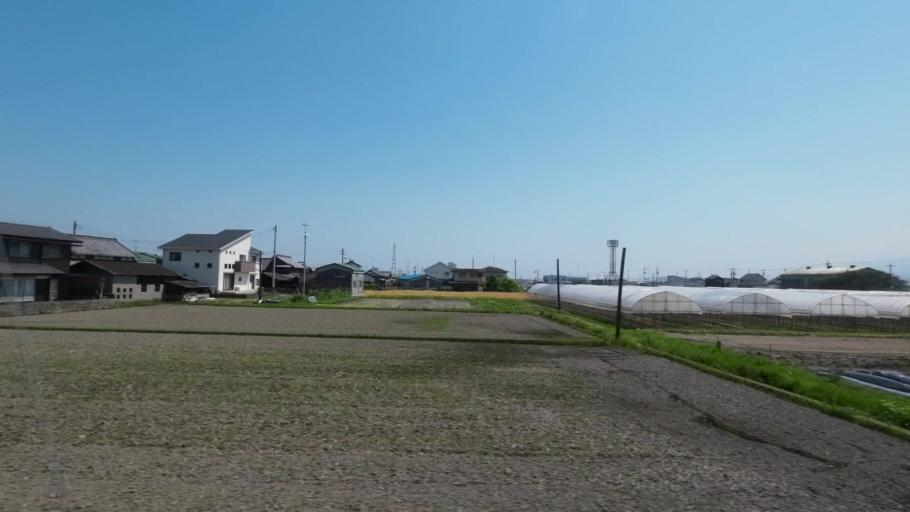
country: JP
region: Ehime
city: Saijo
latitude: 33.9189
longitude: 133.0951
